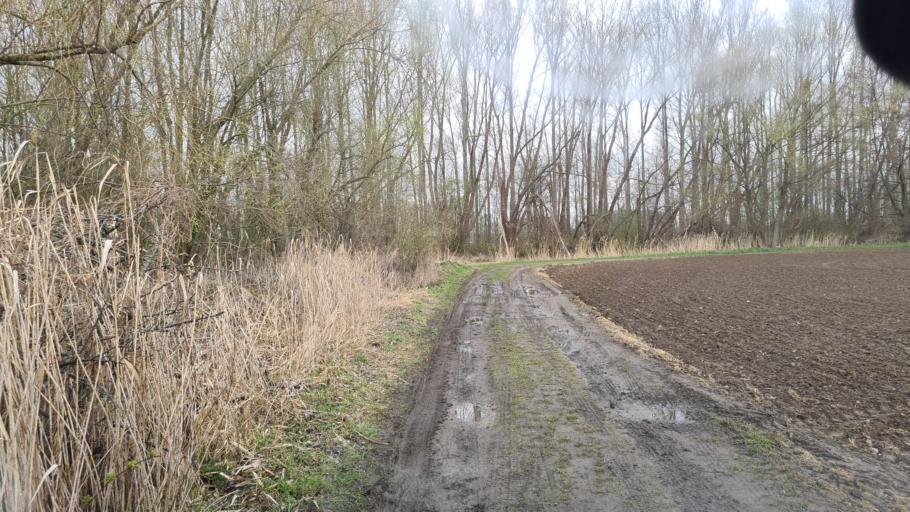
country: DE
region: Brandenburg
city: Doberlug-Kirchhain
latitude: 51.6474
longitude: 13.5580
